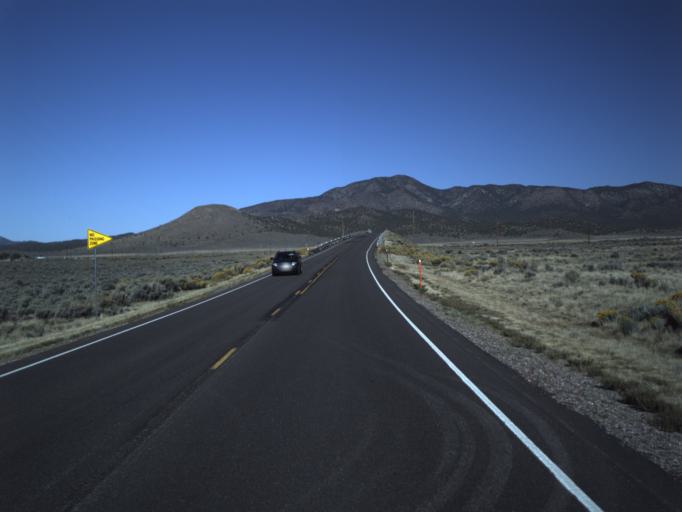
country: US
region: Utah
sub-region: Washington County
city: Enterprise
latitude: 37.7992
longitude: -113.9122
